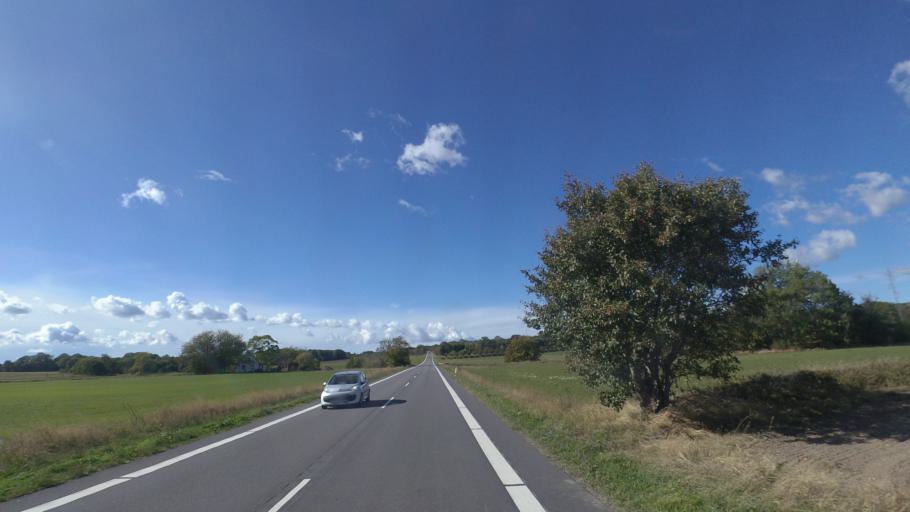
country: DK
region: Capital Region
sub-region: Bornholm Kommune
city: Nexo
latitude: 55.0609
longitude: 15.0456
